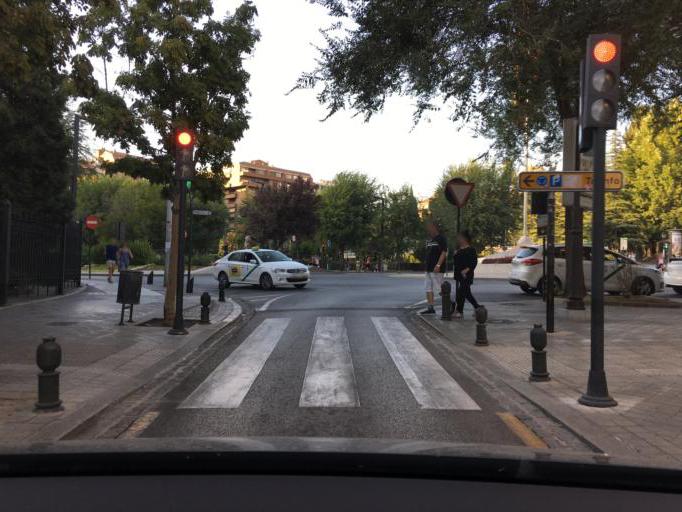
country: ES
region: Andalusia
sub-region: Provincia de Granada
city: Granada
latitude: 37.1826
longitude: -3.6024
